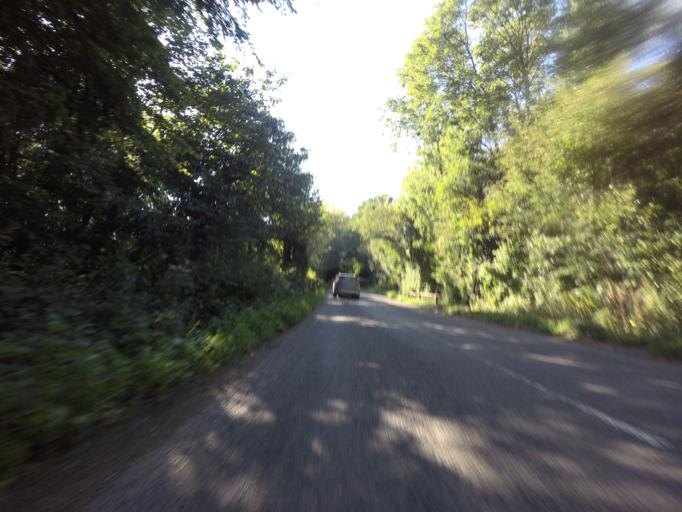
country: GB
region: England
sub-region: Kent
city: Tenterden
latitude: 51.0485
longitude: 0.6957
